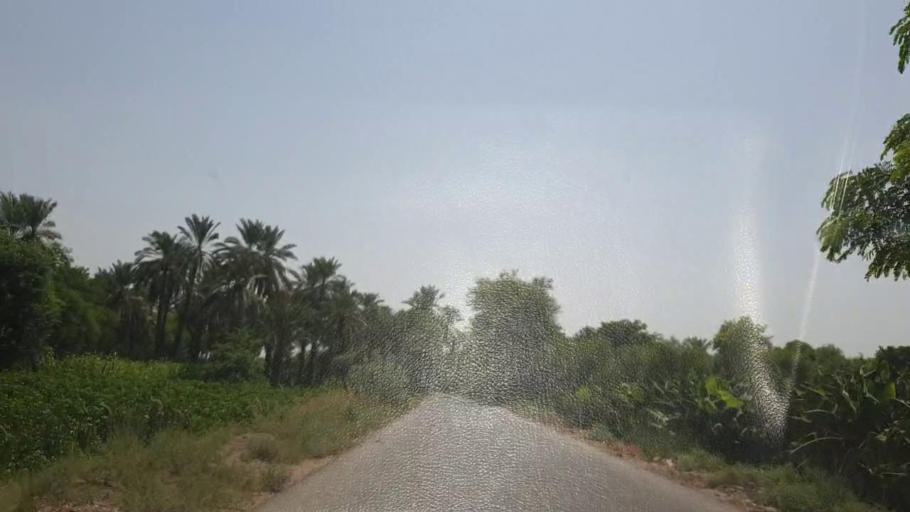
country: PK
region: Sindh
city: Kot Diji
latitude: 27.2818
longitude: 68.6391
